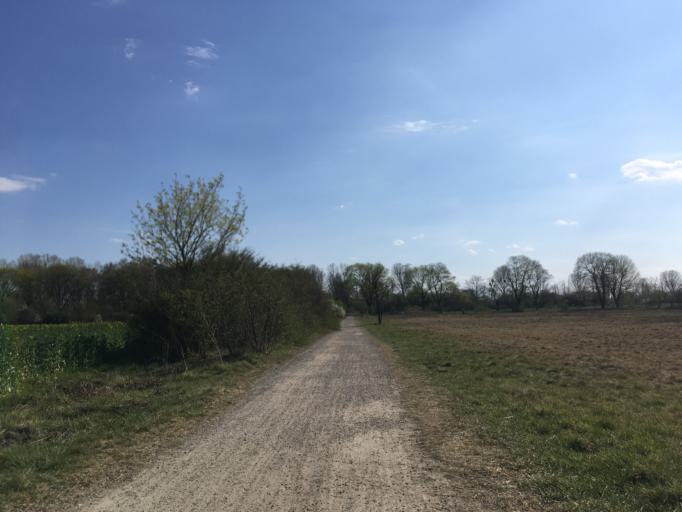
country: DE
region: Berlin
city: Karow
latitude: 52.5969
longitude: 13.4974
